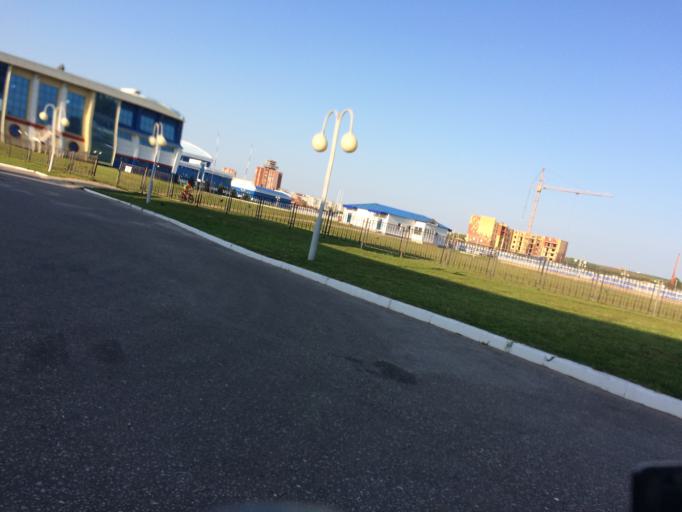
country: RU
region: Mariy-El
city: Yoshkar-Ola
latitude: 56.6221
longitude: 47.8917
